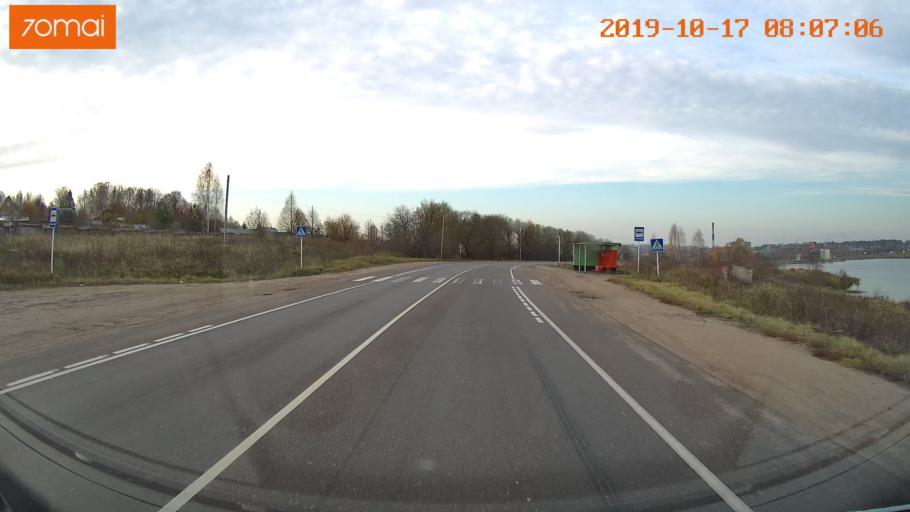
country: RU
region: Vladimir
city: Kol'chugino
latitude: 56.3178
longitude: 39.4028
